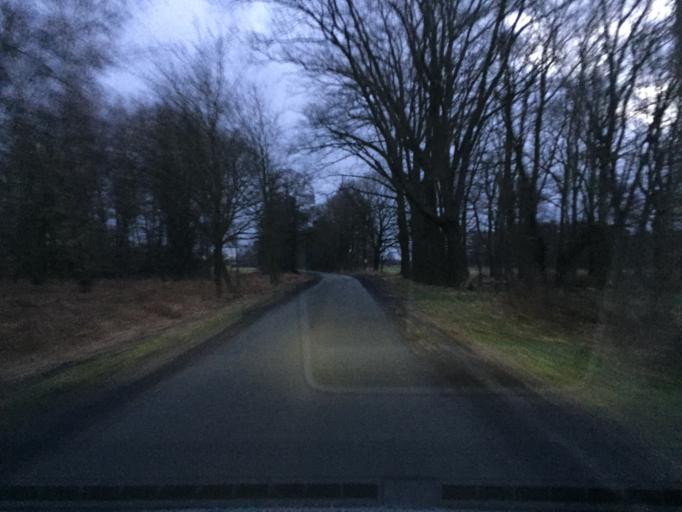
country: DE
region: Lower Saxony
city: Kirchdorf
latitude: 52.6297
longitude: 8.8738
